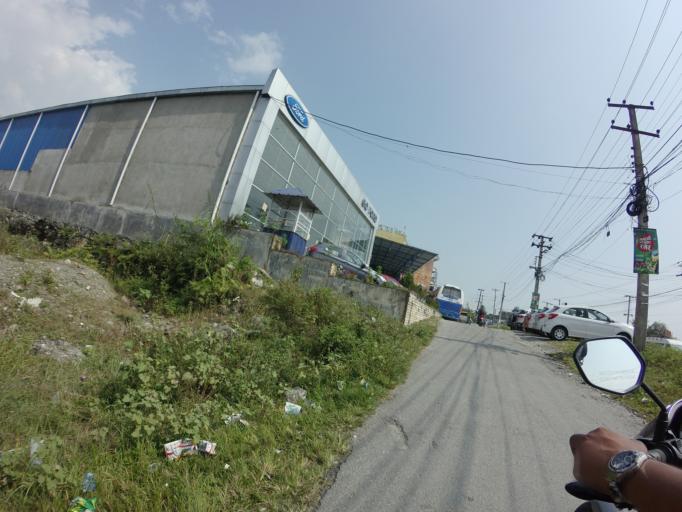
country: NP
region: Western Region
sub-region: Gandaki Zone
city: Pokhara
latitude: 28.2071
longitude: 83.9916
